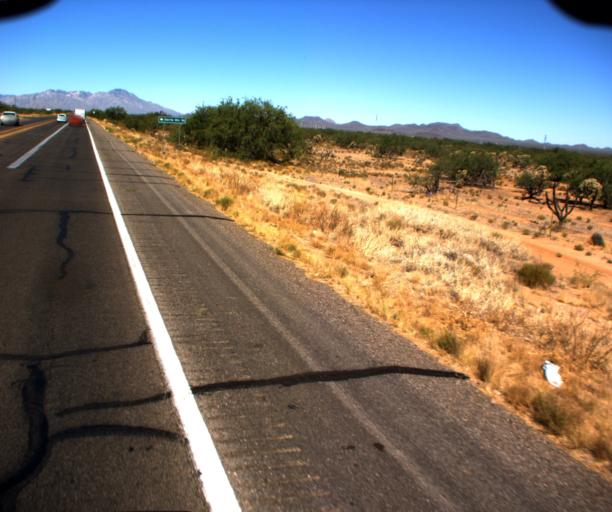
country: US
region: Arizona
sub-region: Pima County
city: Three Points
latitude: 32.0965
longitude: -111.2639
